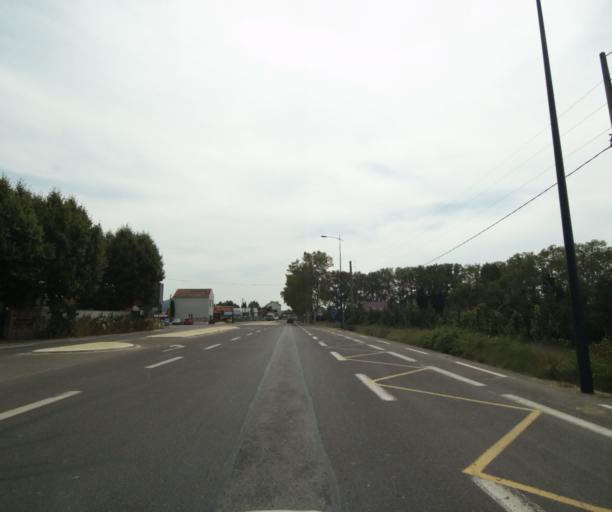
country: FR
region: Provence-Alpes-Cote d'Azur
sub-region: Departement du Var
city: La Garde
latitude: 43.1348
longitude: 6.0348
